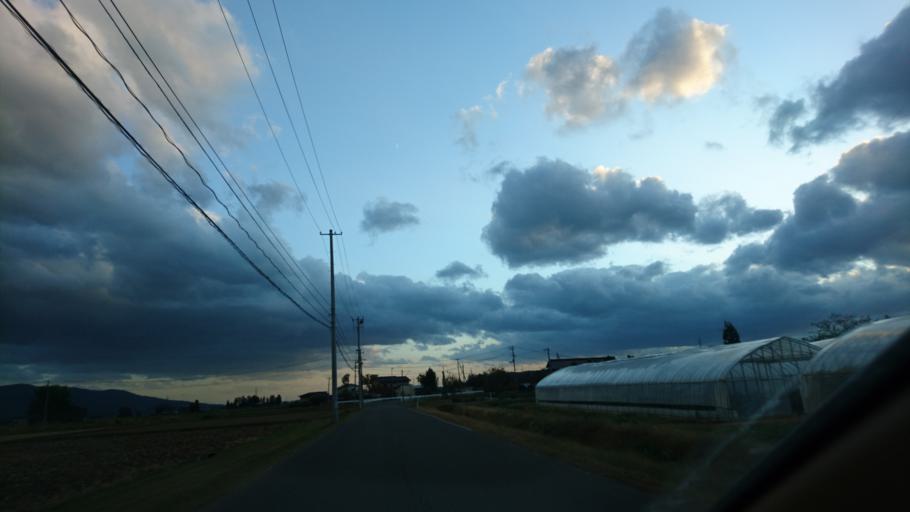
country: JP
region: Iwate
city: Mizusawa
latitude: 39.0972
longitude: 141.1453
